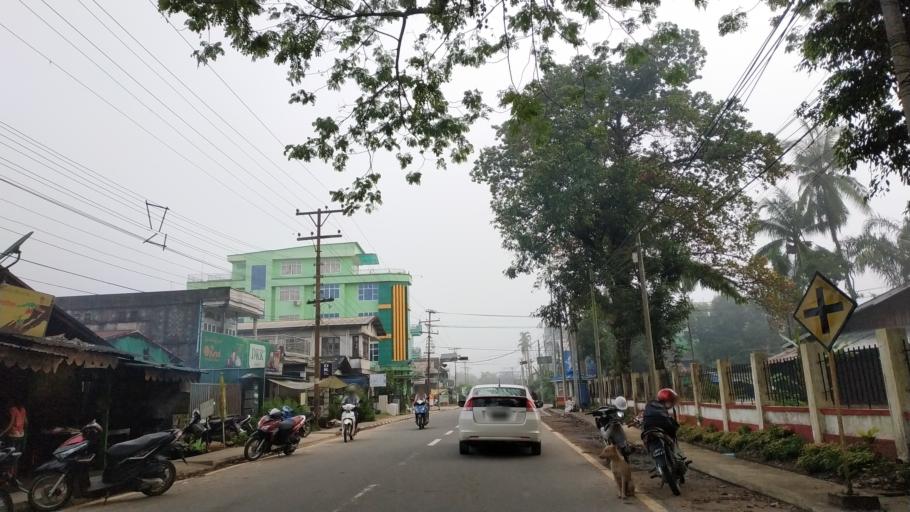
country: MM
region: Tanintharyi
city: Dawei
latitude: 14.0835
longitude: 98.1944
